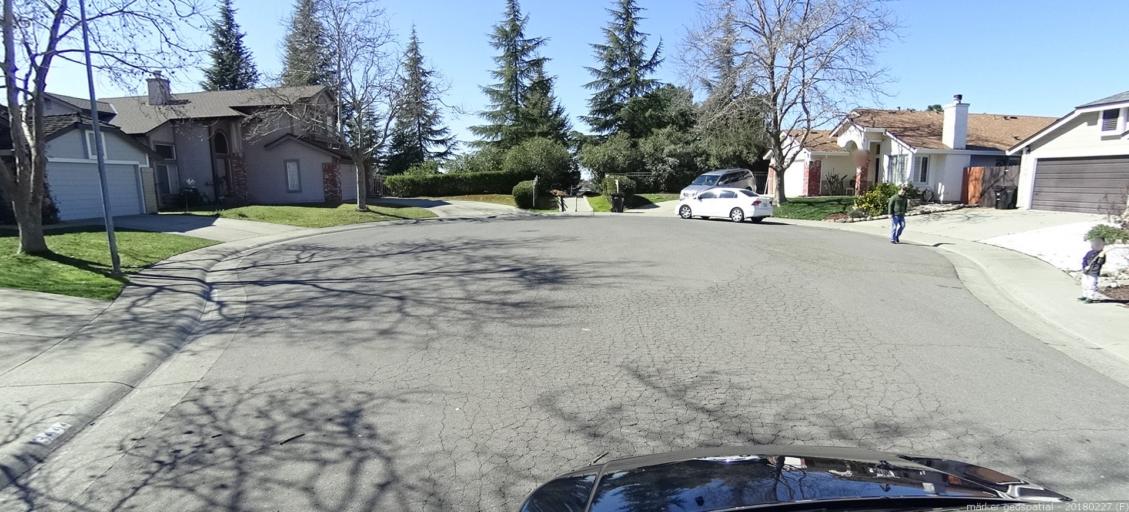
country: US
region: California
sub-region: Sacramento County
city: North Highlands
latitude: 38.7197
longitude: -121.3826
